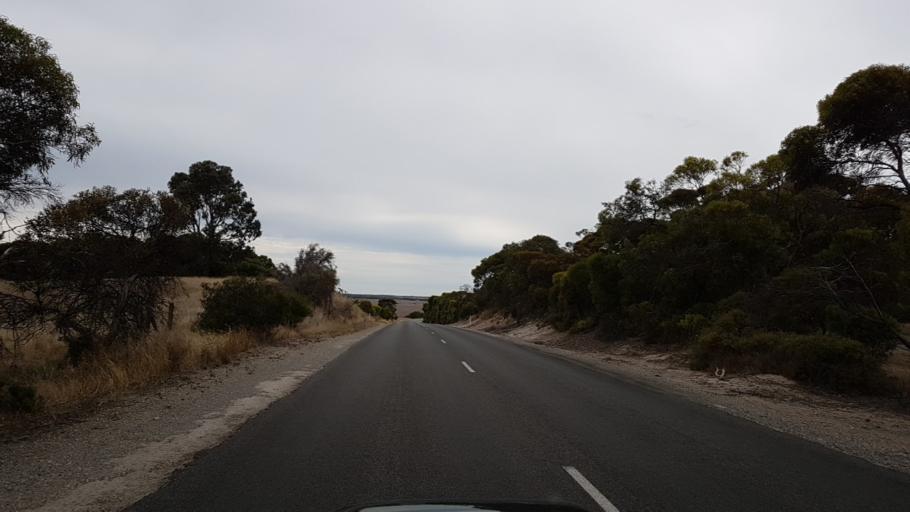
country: AU
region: South Australia
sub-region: Yorke Peninsula
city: Honiton
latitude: -34.9856
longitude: 137.1584
